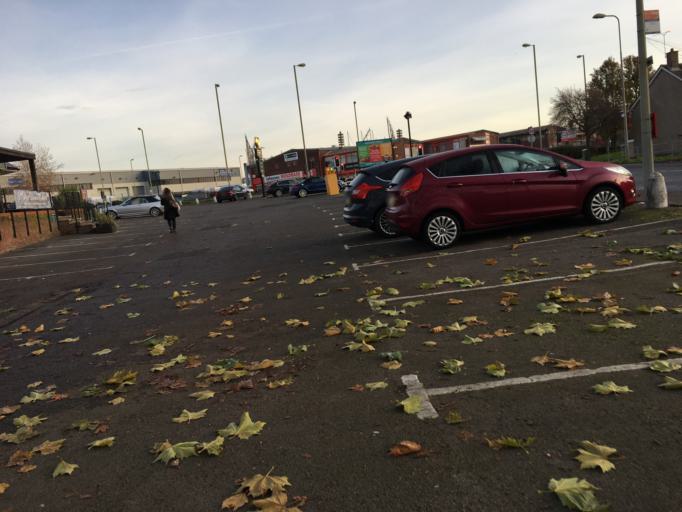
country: GB
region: England
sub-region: Oxfordshire
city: Cowley
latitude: 51.7249
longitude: -1.1932
